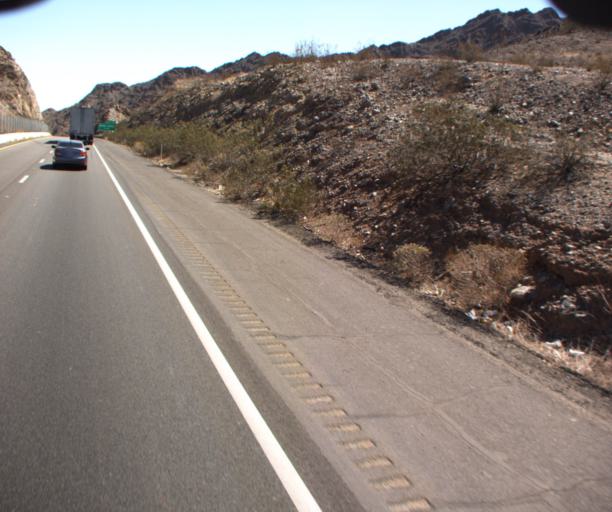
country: US
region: Arizona
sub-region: Yuma County
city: Fortuna Foothills
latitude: 32.6604
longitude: -114.3272
